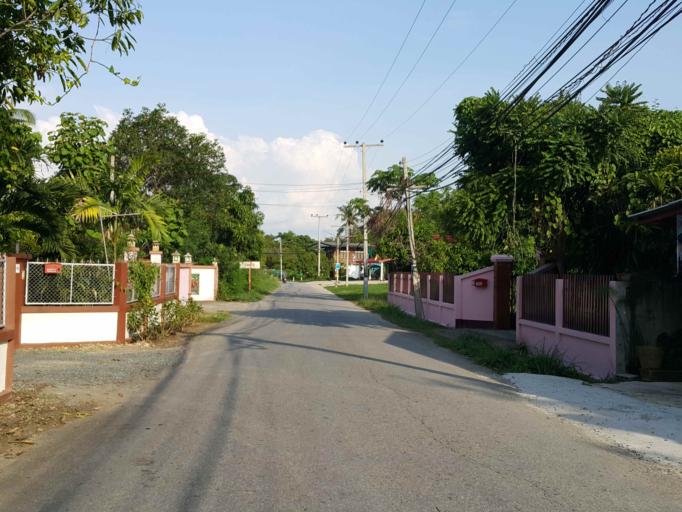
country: TH
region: Chiang Mai
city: San Sai
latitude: 18.8448
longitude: 99.0980
